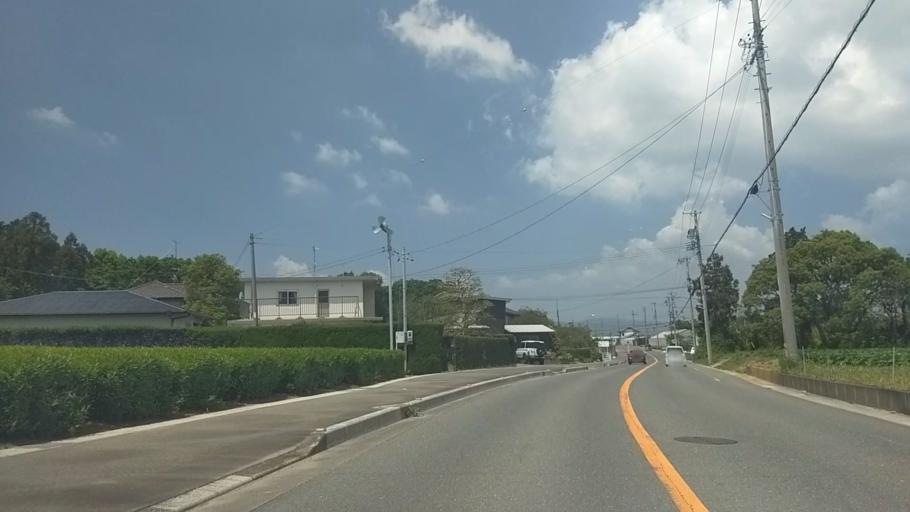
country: JP
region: Shizuoka
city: Hamamatsu
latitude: 34.7542
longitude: 137.6813
